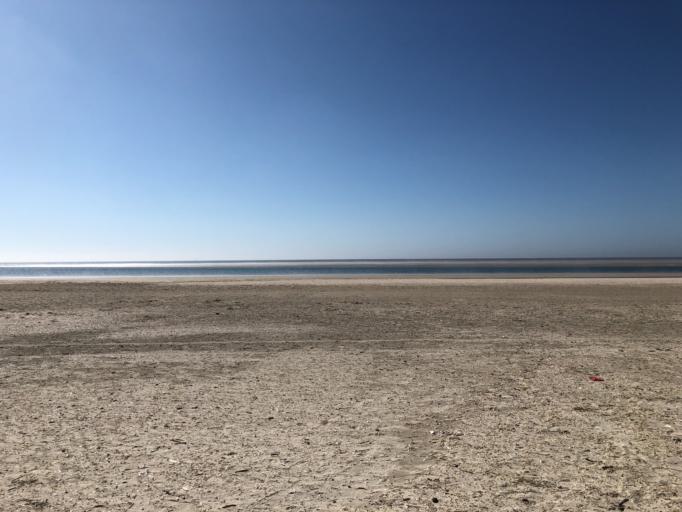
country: DK
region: South Denmark
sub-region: Varde Kommune
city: Oksbol
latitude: 55.5546
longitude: 8.0858
